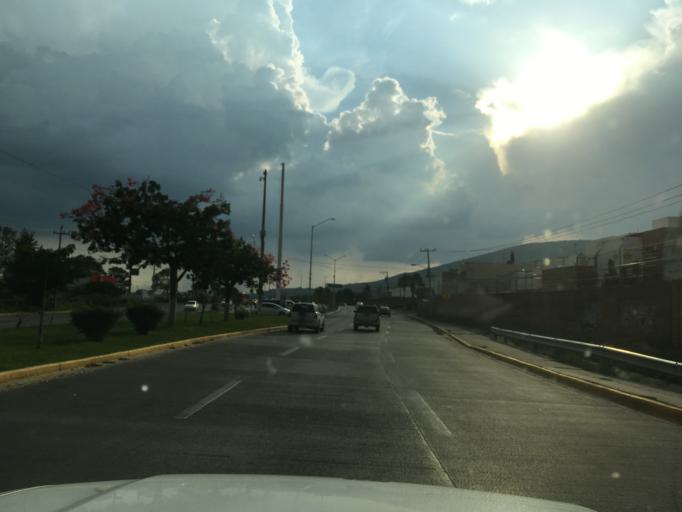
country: MX
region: Jalisco
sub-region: Tlajomulco de Zuniga
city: Santa Cruz de las Flores
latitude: 20.4905
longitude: -103.4860
